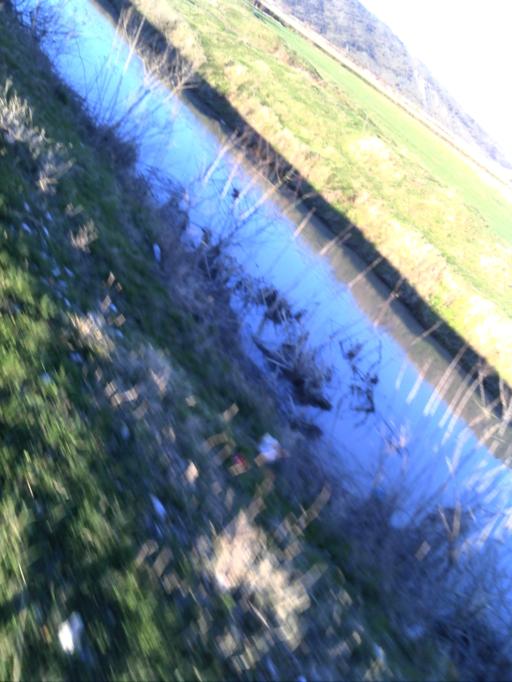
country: AL
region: Shkoder
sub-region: Rrethi i Shkodres
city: Dajc
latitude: 41.9422
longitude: 19.4459
